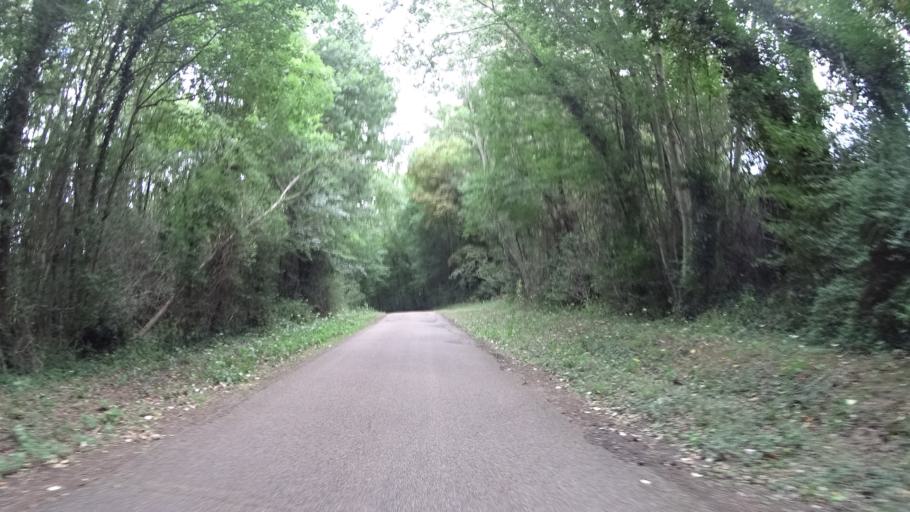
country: FR
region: Centre
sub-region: Departement du Loiret
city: Saint-Germain-des-Pres
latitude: 47.9438
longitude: 2.8278
